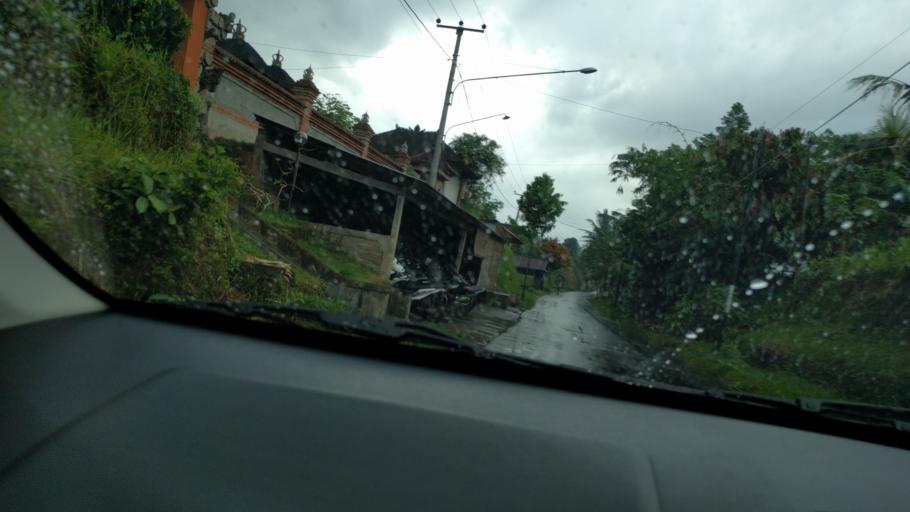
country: ID
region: Bali
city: Bunutan
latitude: -8.4775
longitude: 115.2589
